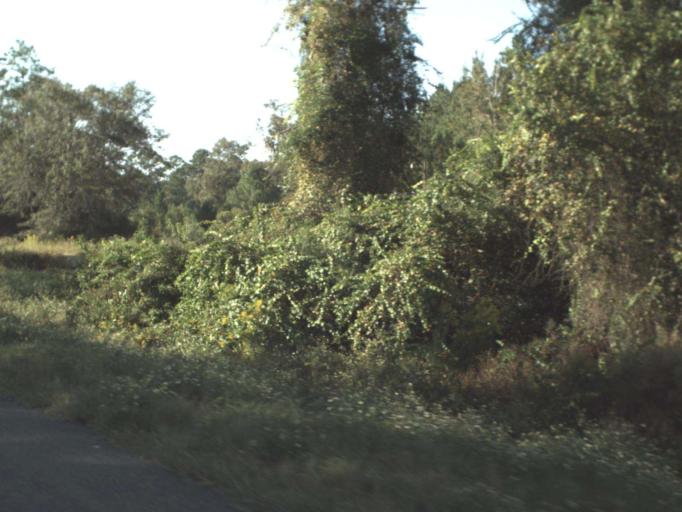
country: US
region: Florida
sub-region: Bay County
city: Laguna Beach
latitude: 30.4467
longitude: -85.8852
